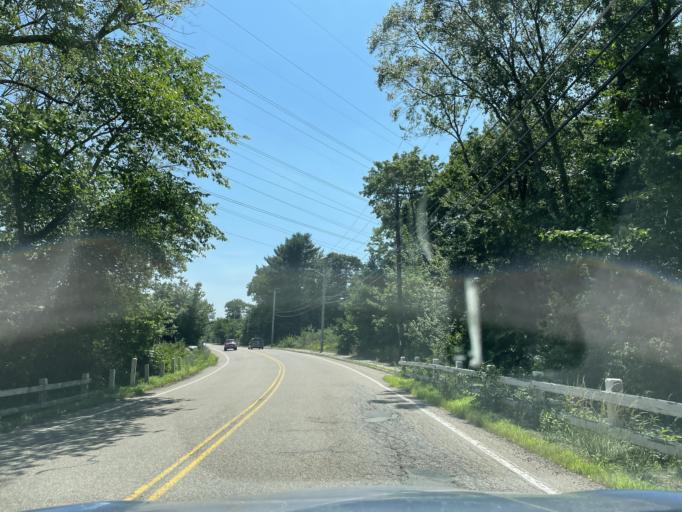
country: US
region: Massachusetts
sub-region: Norfolk County
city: Randolph
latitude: 42.1589
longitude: -71.0256
